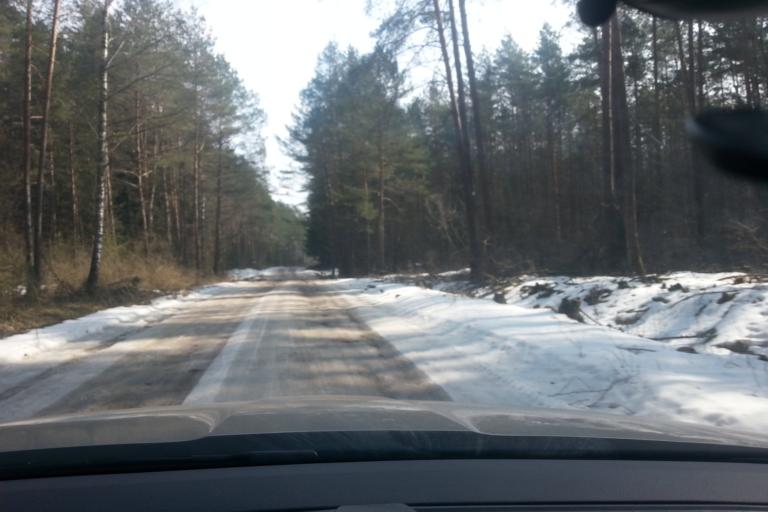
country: LT
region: Vilnius County
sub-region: Trakai
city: Rudiskes
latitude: 54.5093
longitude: 24.9381
